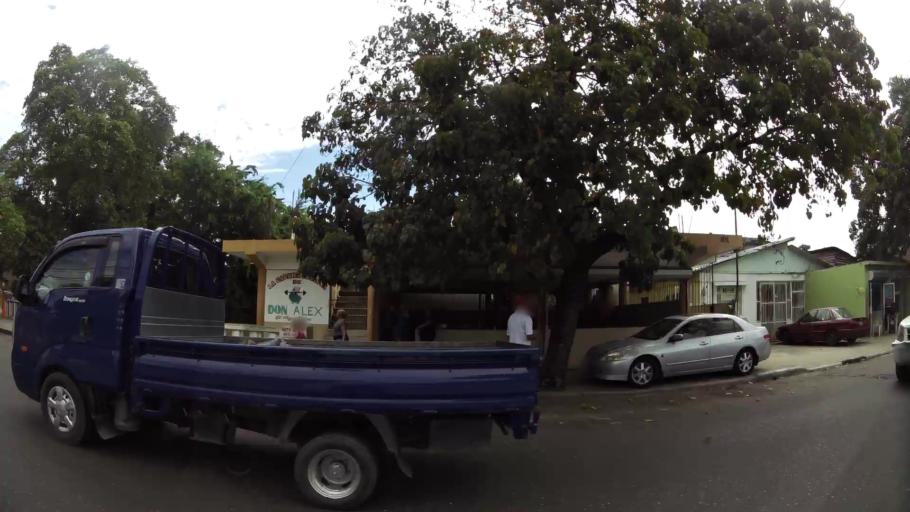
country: DO
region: Santiago
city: Santiago de los Caballeros
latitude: 19.4627
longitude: -70.7120
